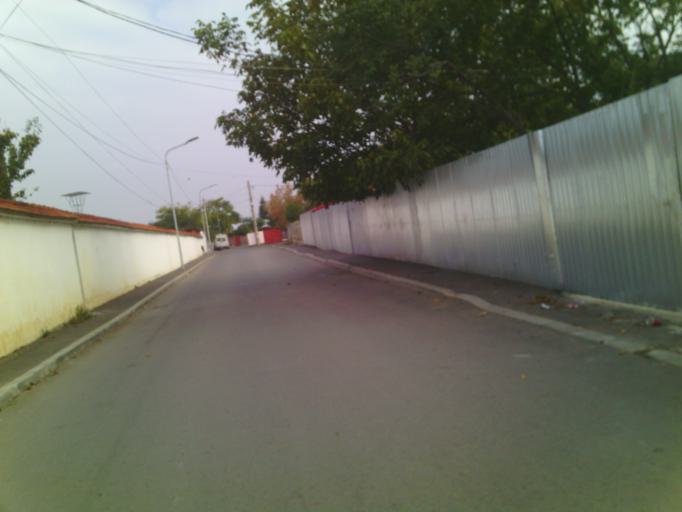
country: RO
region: Bucuresti
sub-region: Municipiul Bucuresti
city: Bucuresti
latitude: 44.3899
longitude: 26.0673
